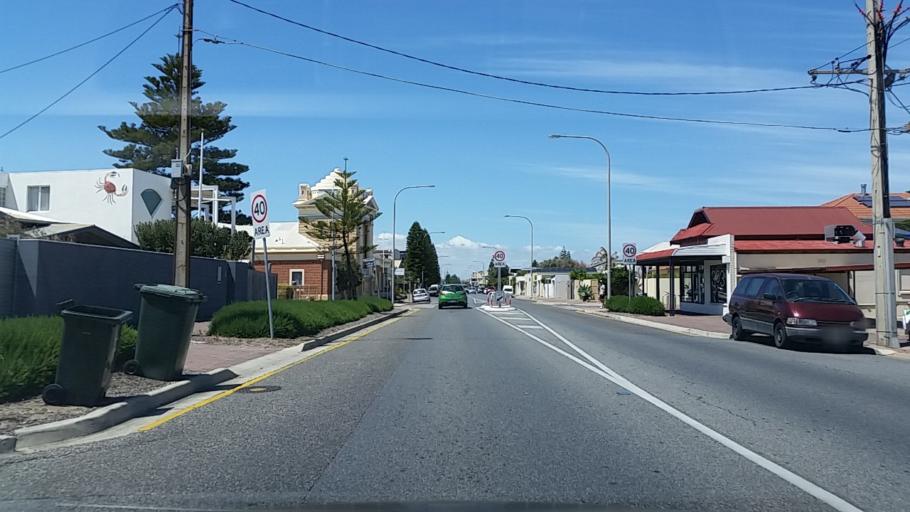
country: AU
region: South Australia
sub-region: Charles Sturt
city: Henley Beach
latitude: -34.9161
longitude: 138.4934
